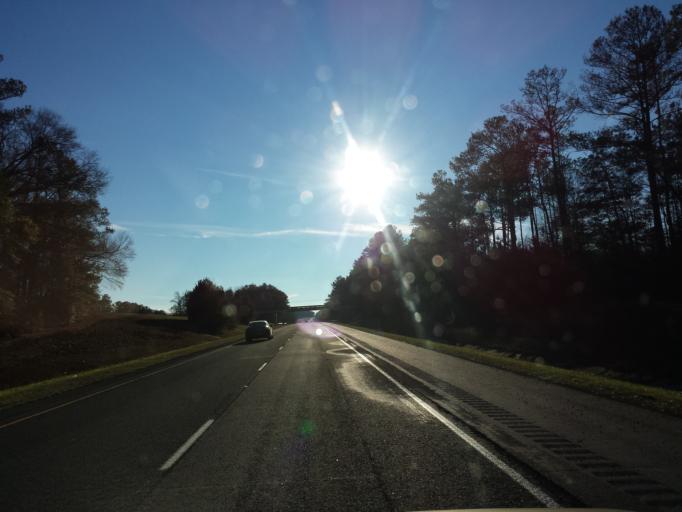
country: US
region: Alabama
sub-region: Hale County
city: Moundville
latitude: 33.0069
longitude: -87.7631
